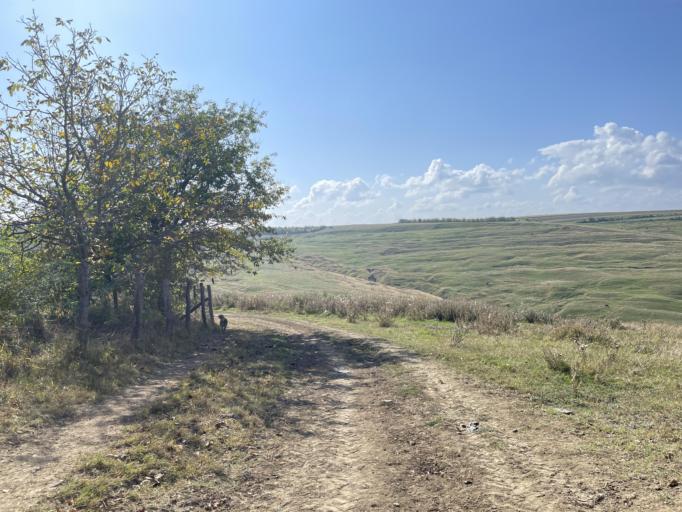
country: RO
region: Iasi
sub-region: Comuna Dumesti
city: Pausesti
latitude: 47.1555
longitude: 27.3136
